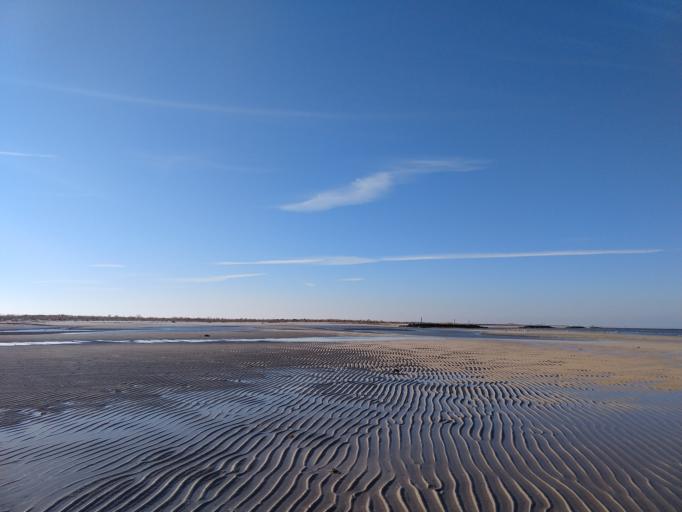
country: US
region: Virginia
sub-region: City of Poquoson
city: Poquoson
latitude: 37.1025
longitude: -76.2840
